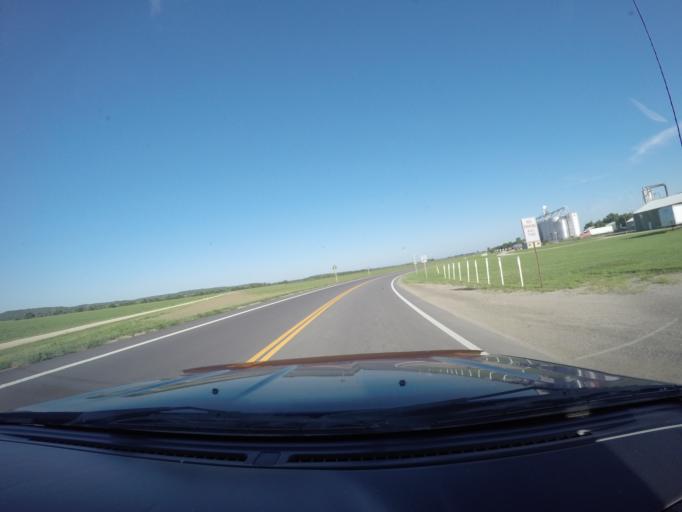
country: US
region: Kansas
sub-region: Douglas County
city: Lawrence
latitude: 39.0296
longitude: -95.2412
